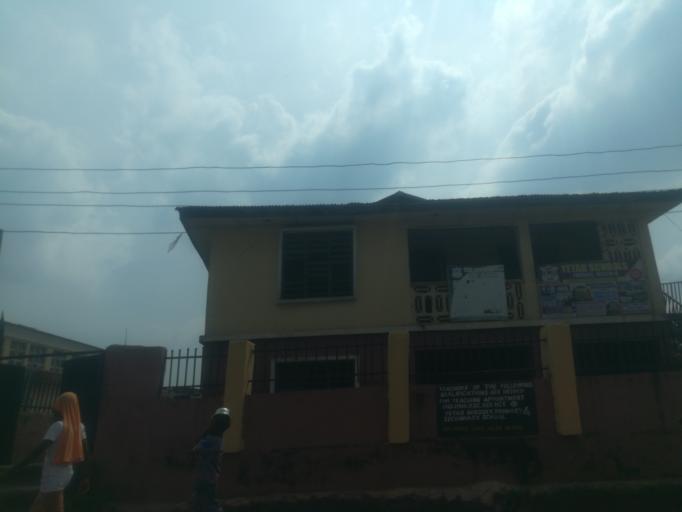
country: NG
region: Oyo
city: Ibadan
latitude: 7.3952
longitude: 3.9081
